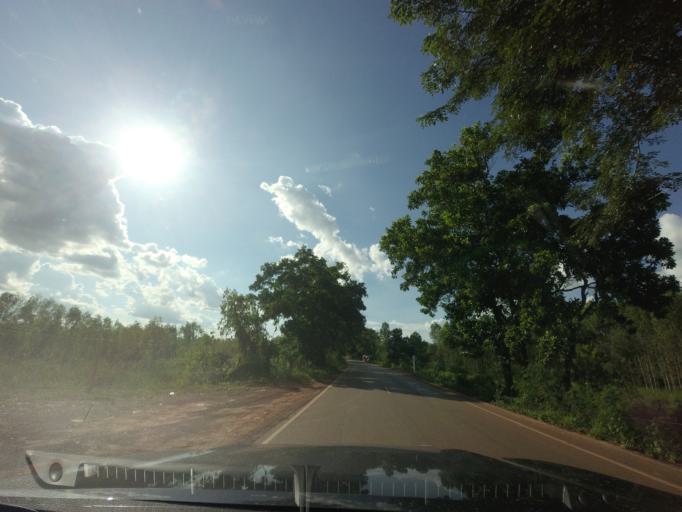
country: TH
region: Changwat Udon Thani
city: Ban Dung
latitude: 17.7435
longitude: 103.3386
